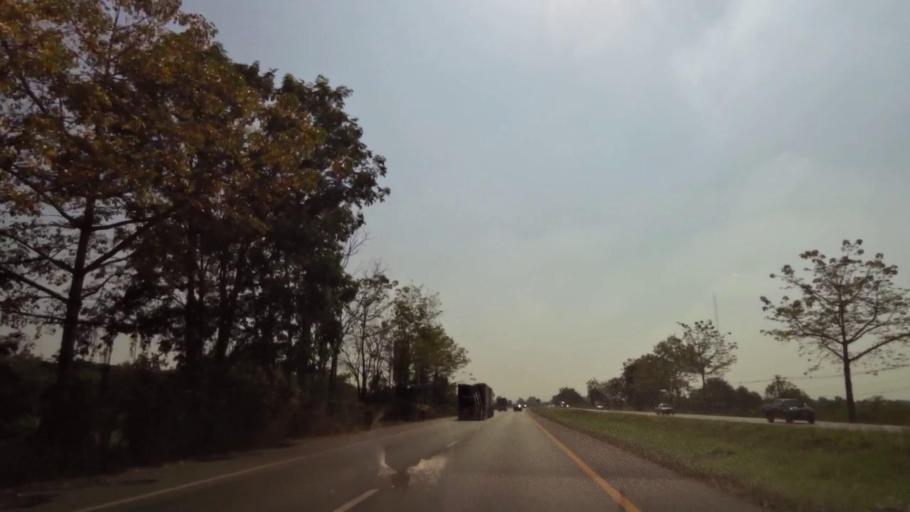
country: TH
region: Phichit
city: Wachira Barami
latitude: 16.4793
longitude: 100.1469
